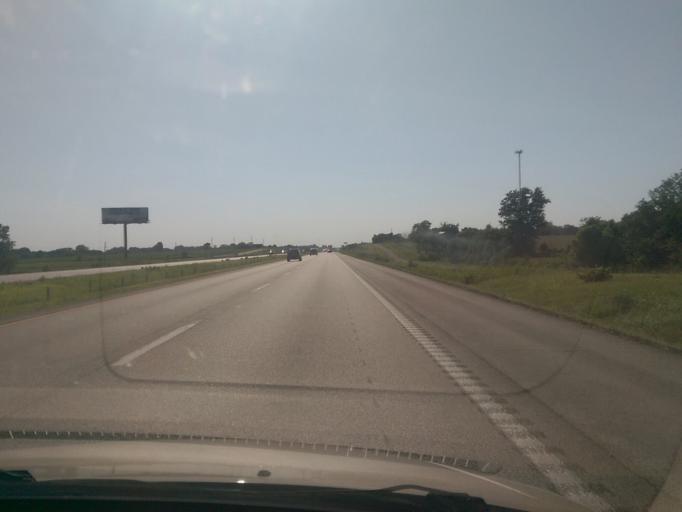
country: US
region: Missouri
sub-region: Saline County
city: Sweet Springs
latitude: 38.9740
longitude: -93.3432
